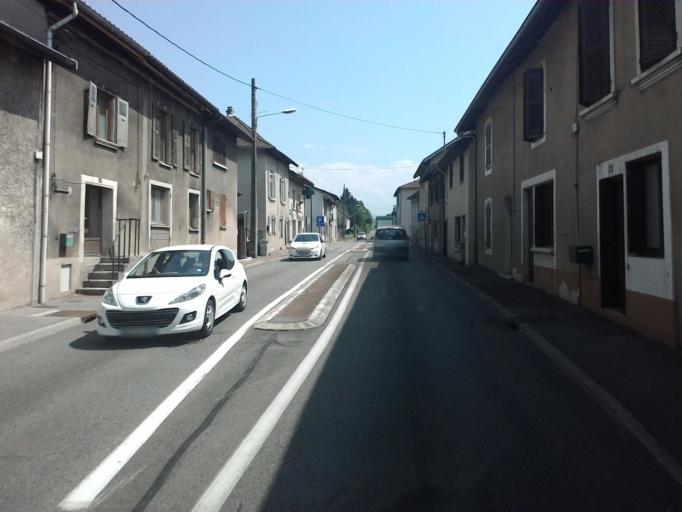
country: FR
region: Rhone-Alpes
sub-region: Departement de l'Isere
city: Chirens
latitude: 45.4121
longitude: 5.5581
